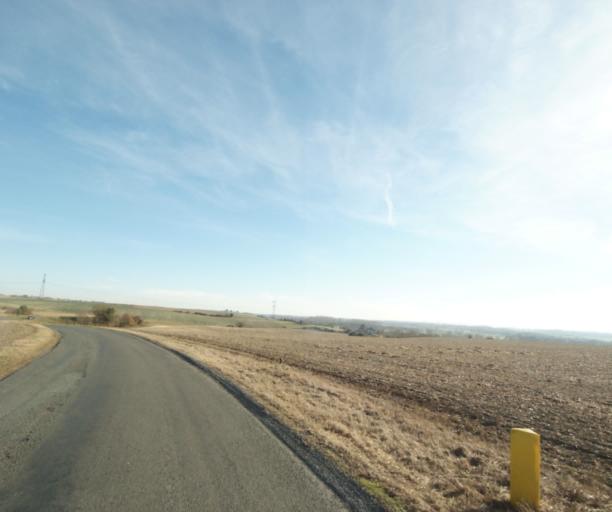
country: FR
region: Poitou-Charentes
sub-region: Departement de la Charente-Maritime
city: Les Gonds
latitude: 45.7327
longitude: -0.5925
